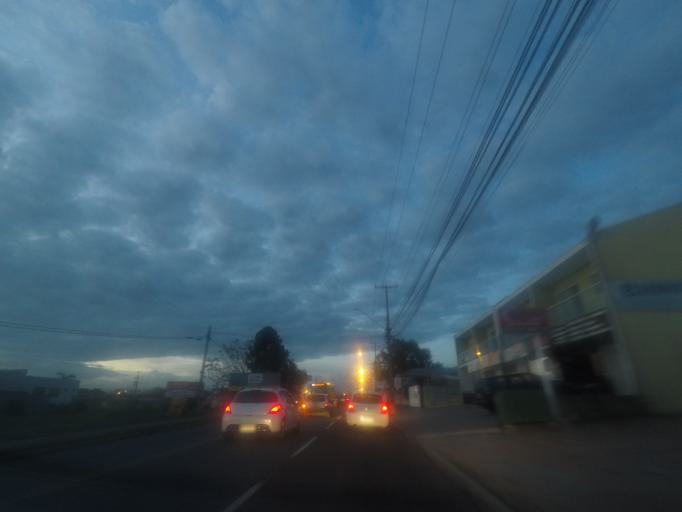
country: BR
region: Parana
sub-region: Pinhais
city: Pinhais
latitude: -25.4044
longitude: -49.1897
